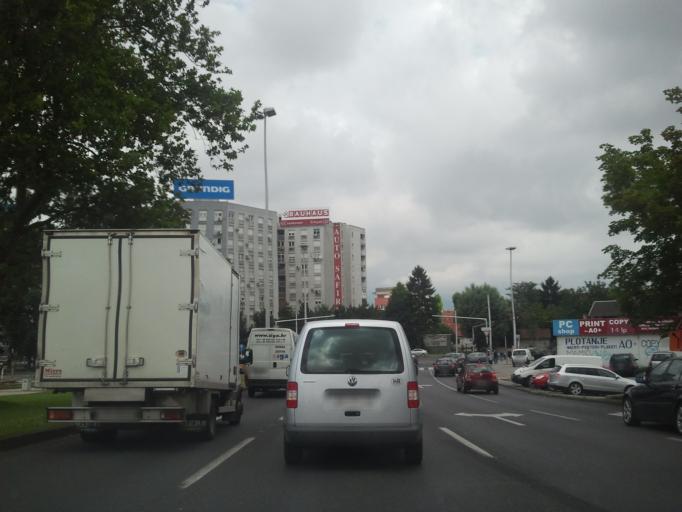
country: HR
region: Grad Zagreb
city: Novi Zagreb
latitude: 45.7857
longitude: 15.9520
